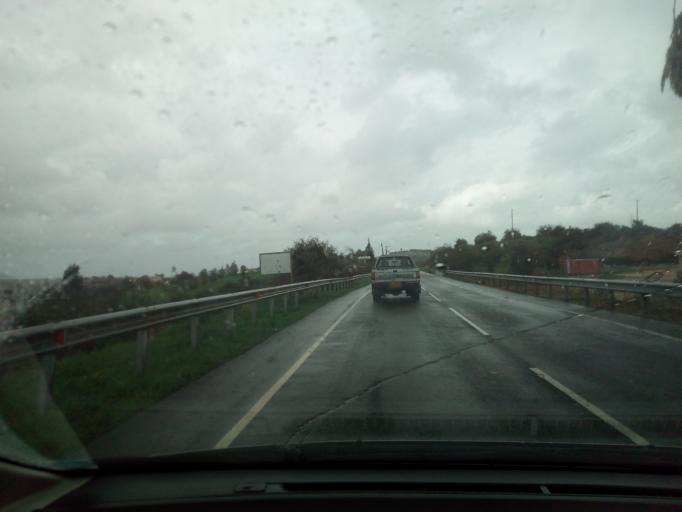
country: CY
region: Pafos
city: Polis
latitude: 34.9994
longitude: 32.4451
